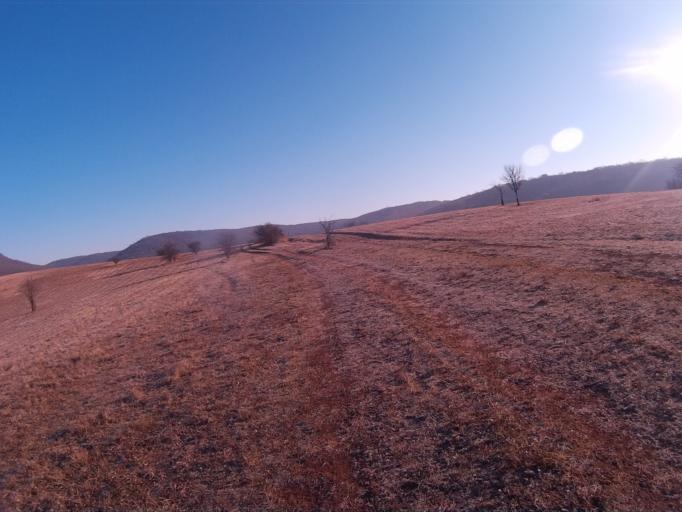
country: HU
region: Borsod-Abauj-Zemplen
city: Rudabanya
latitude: 48.4928
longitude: 20.5522
